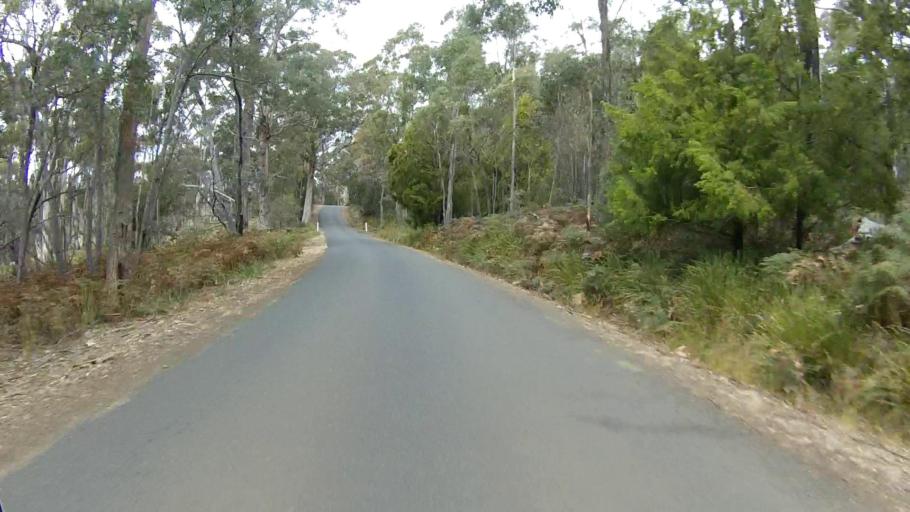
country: AU
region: Tasmania
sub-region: Sorell
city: Sorell
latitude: -42.6050
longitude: 147.9220
